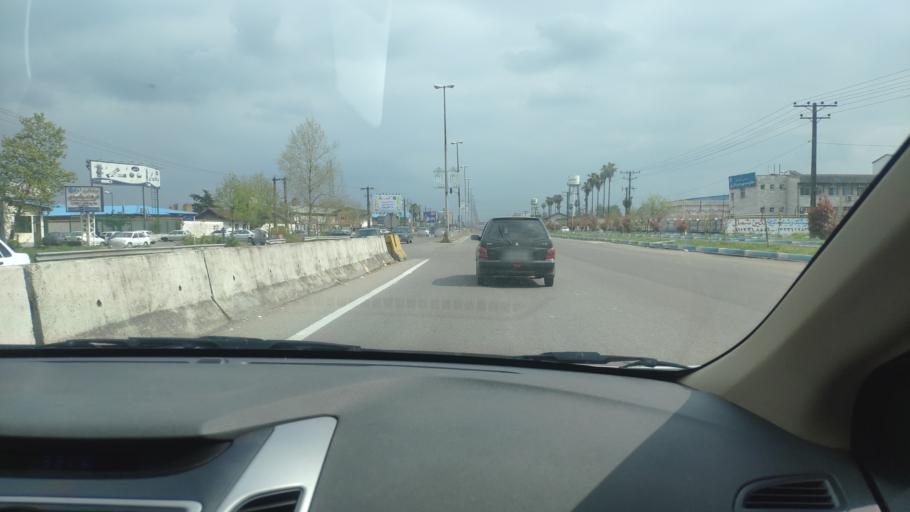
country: IR
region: Gilan
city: Rasht
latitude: 37.2350
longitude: 49.6270
